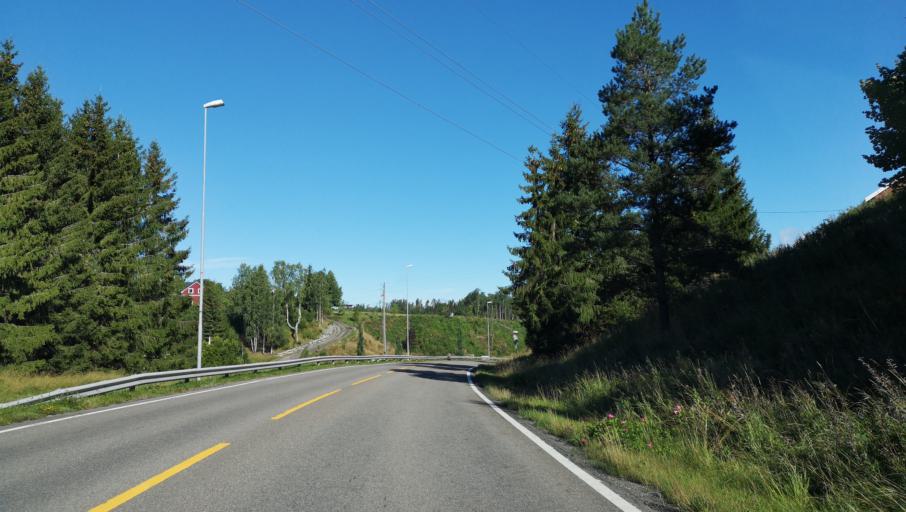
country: NO
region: Ostfold
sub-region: Spydeberg
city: Spydeberg
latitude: 59.5970
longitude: 11.1050
